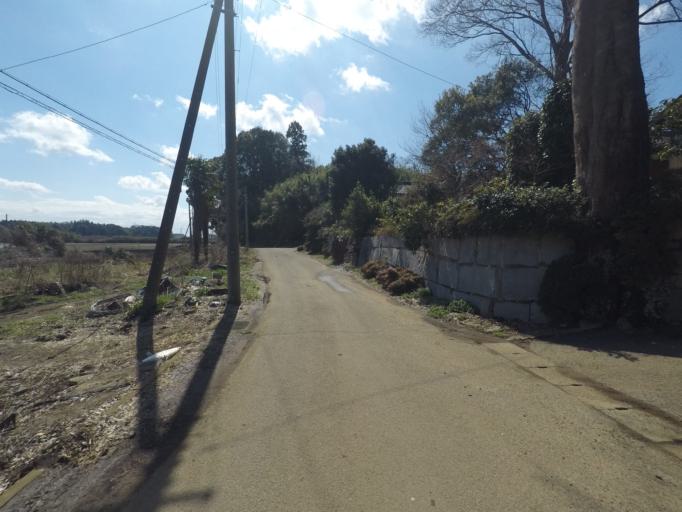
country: JP
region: Ibaraki
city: Ushiku
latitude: 36.0132
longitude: 140.0737
